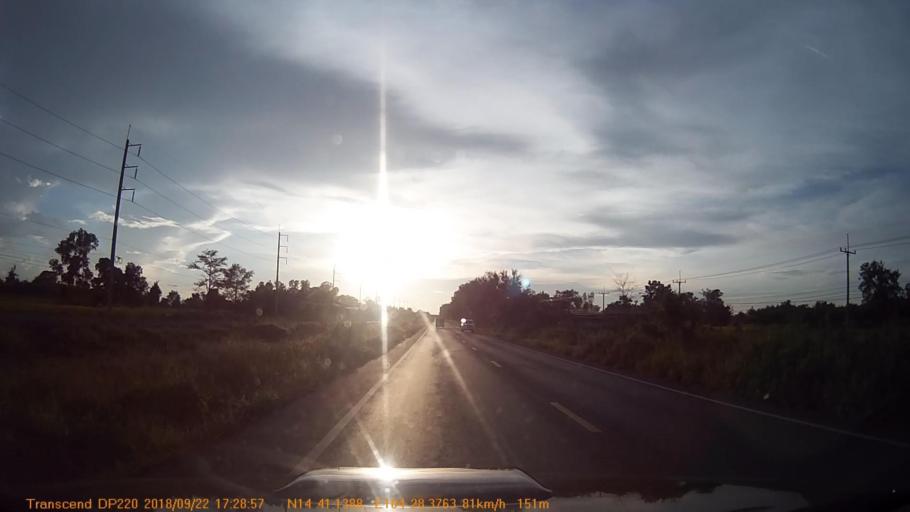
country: TH
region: Sisaket
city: Khun Han
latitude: 14.6858
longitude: 104.4731
